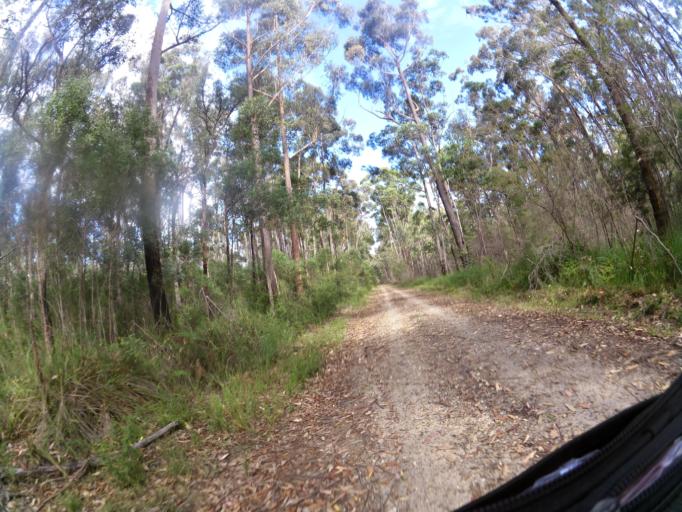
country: AU
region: Victoria
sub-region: East Gippsland
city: Lakes Entrance
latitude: -37.7516
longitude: 148.2107
